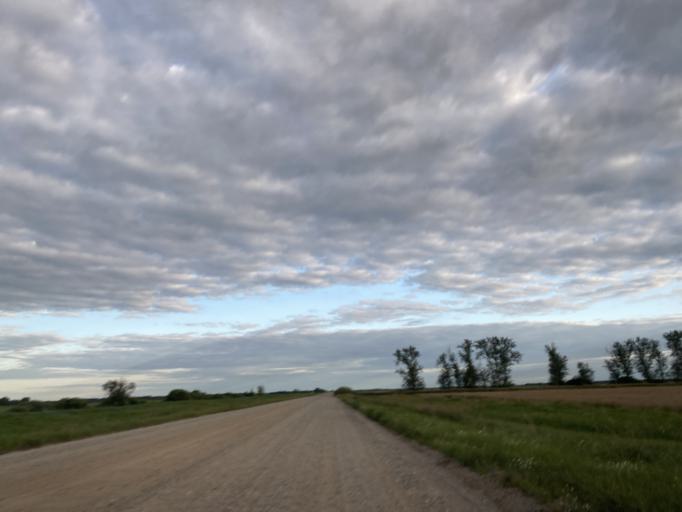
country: BY
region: Brest
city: Tsyelyakhany
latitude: 52.4638
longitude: 25.5713
